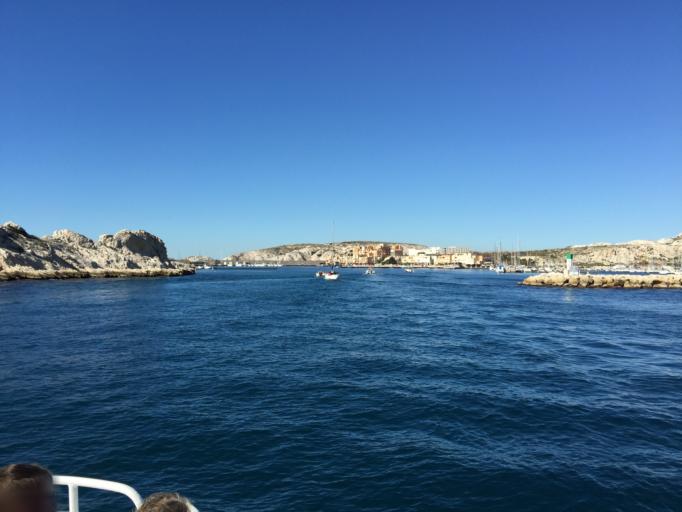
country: FR
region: Provence-Alpes-Cote d'Azur
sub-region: Departement des Bouches-du-Rhone
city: Marseille 07
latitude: 43.2766
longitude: 5.3116
